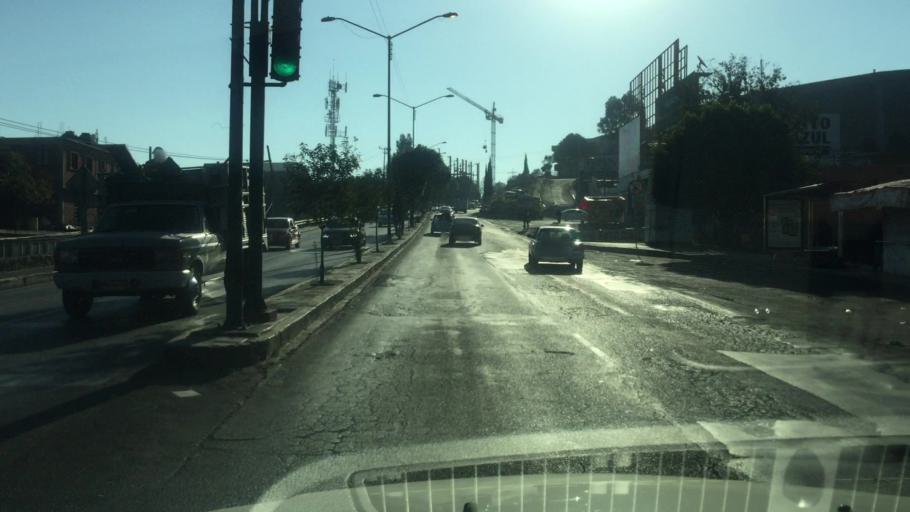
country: MX
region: Mexico City
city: Tlalpan
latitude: 19.2795
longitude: -99.2124
